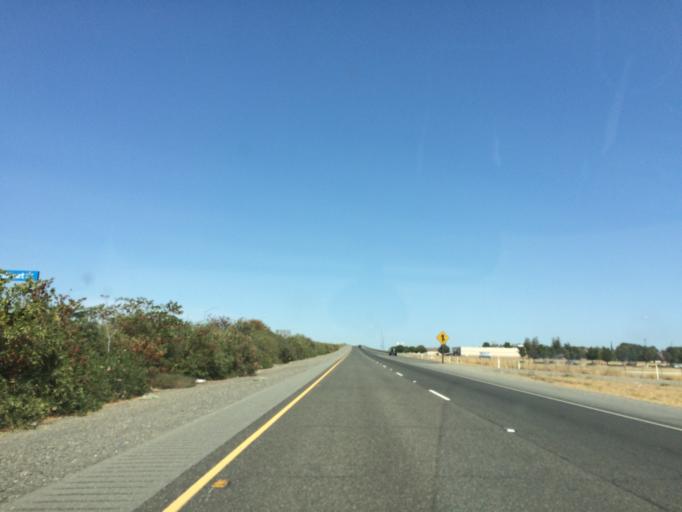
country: US
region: California
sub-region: Glenn County
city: Willows
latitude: 39.5249
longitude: -122.2146
